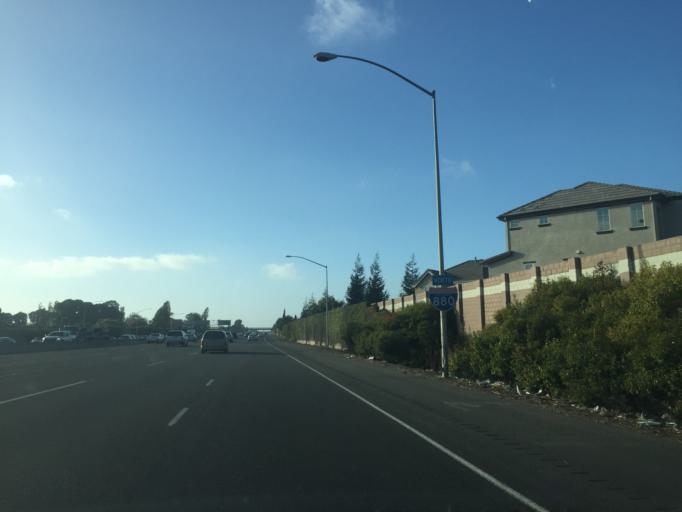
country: US
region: California
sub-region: Alameda County
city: San Lorenzo
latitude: 37.6926
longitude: -122.1404
